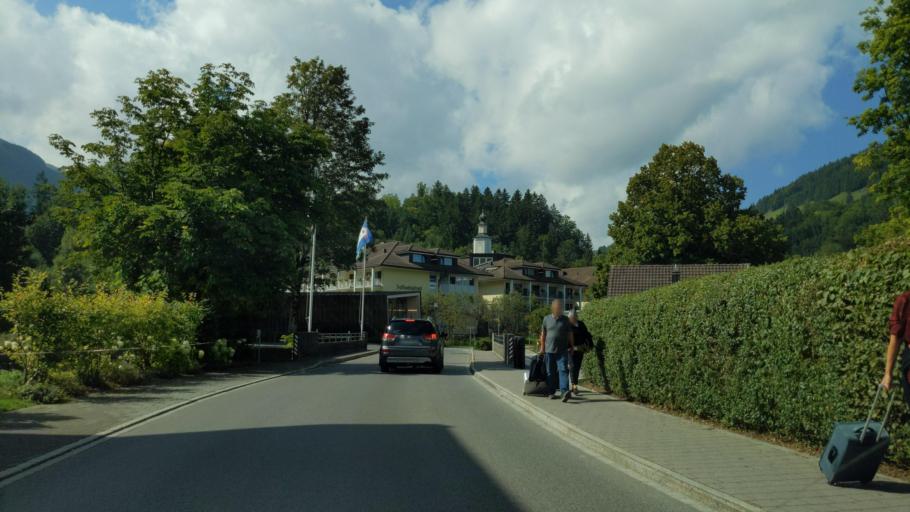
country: CH
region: Appenzell Innerrhoden
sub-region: Appenzell Inner Rhodes
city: Appenzell
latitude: 47.3100
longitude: 9.4345
